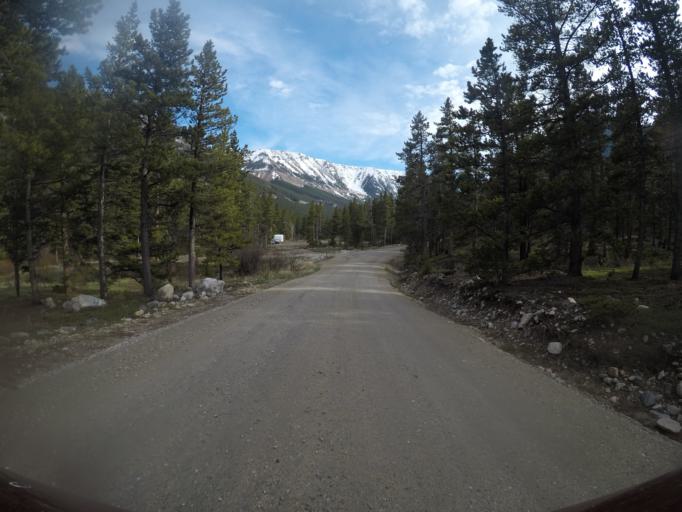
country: US
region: Montana
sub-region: Carbon County
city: Red Lodge
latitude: 45.0468
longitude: -109.4246
